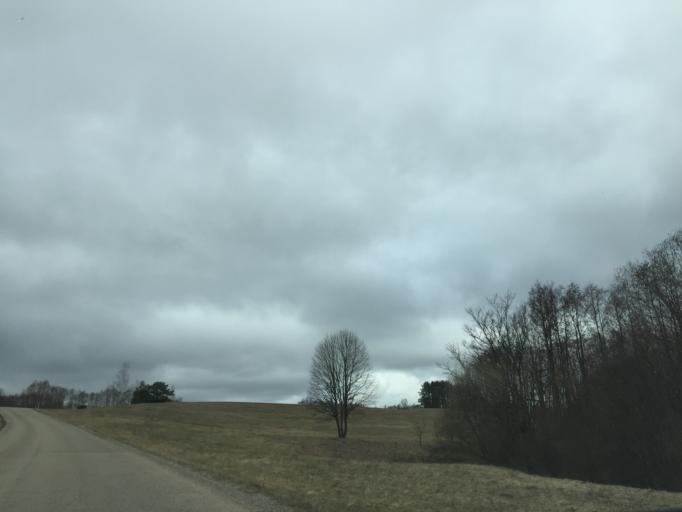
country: LV
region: Ilukste
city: Ilukste
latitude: 56.0421
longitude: 26.1993
